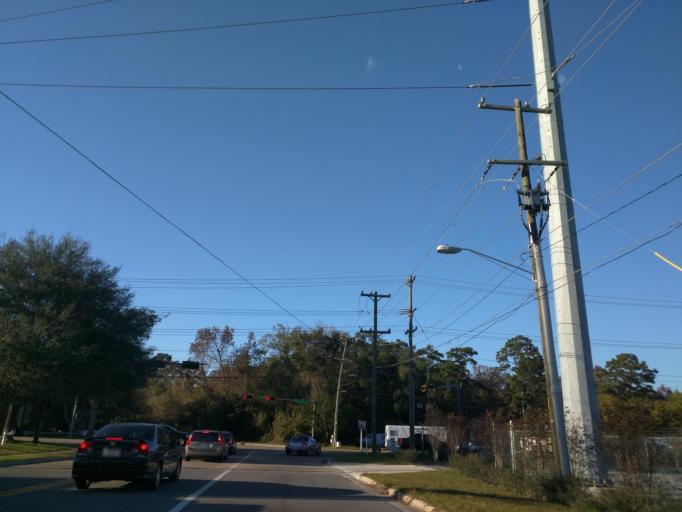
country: US
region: Florida
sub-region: Leon County
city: Tallahassee
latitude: 30.4629
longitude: -84.2406
